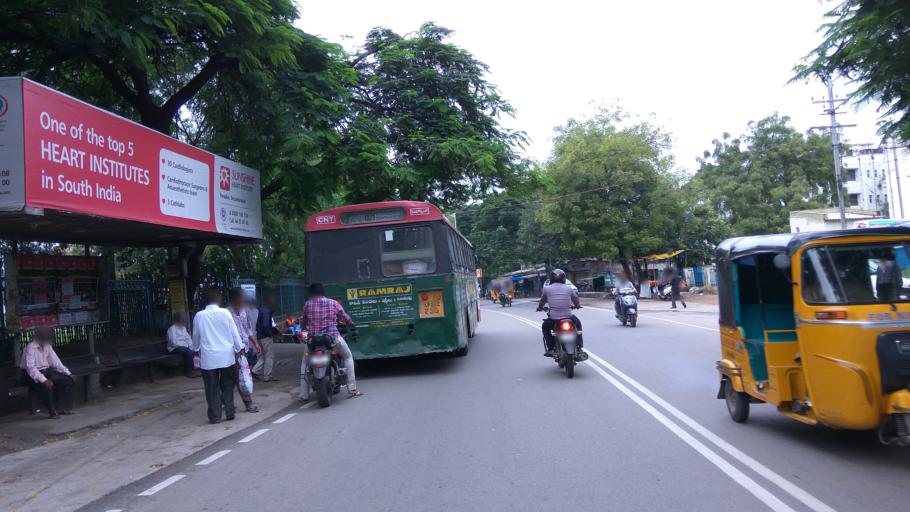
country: IN
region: Telangana
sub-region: Hyderabad
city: Malkajgiri
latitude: 17.4365
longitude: 78.5202
